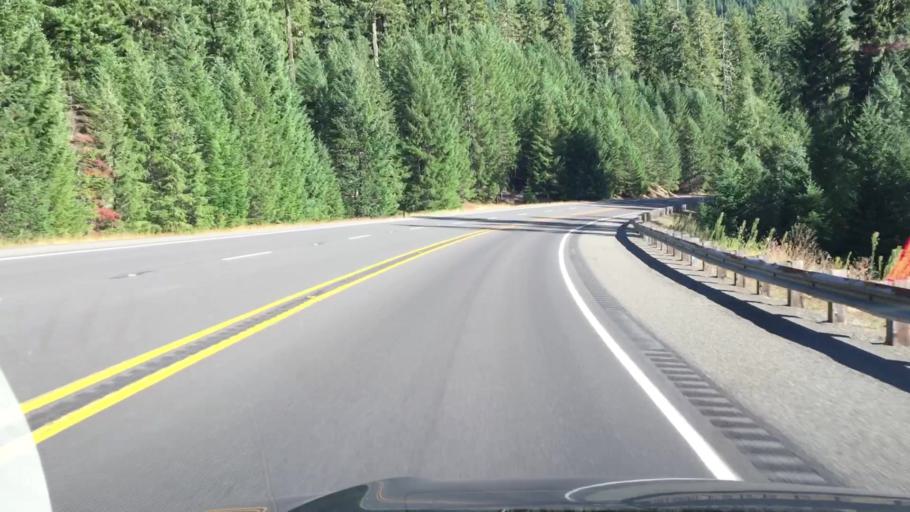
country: US
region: Washington
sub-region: Pierce County
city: Buckley
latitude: 46.6843
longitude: -121.5762
